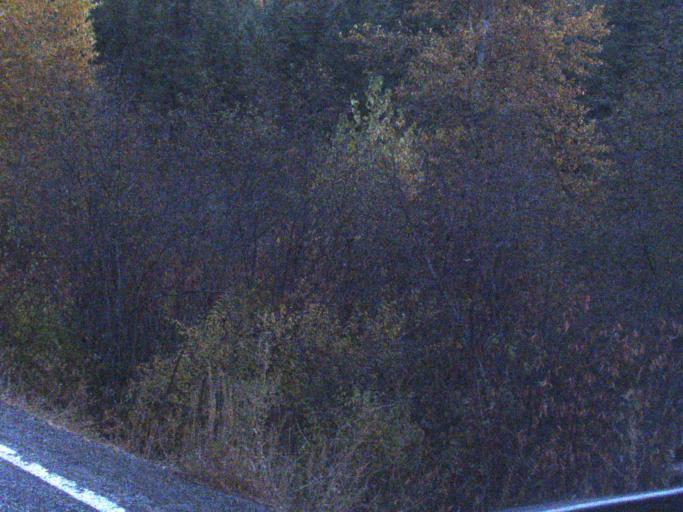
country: US
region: Washington
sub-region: Ferry County
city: Republic
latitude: 48.4758
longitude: -118.7313
